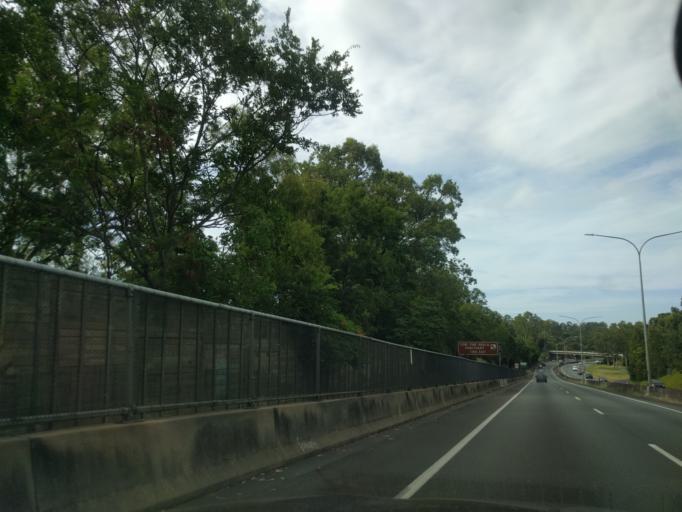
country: AU
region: Queensland
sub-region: Brisbane
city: Kenmore Hills
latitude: -27.5138
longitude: 152.9571
